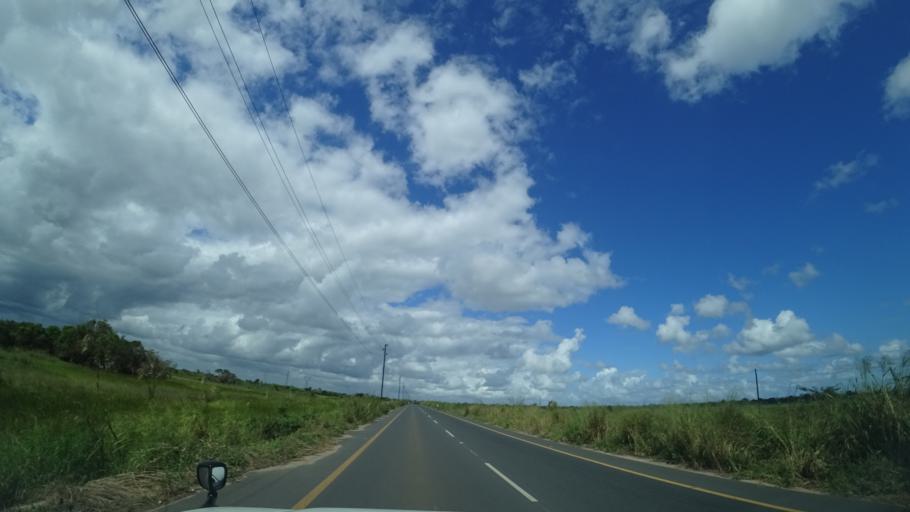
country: MZ
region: Sofala
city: Dondo
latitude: -19.5117
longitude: 34.6134
